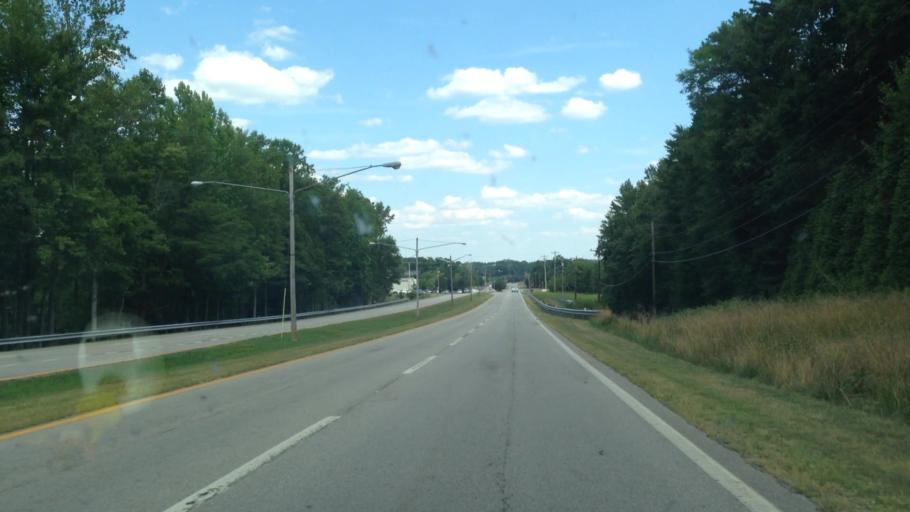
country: US
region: Virginia
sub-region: City of Danville
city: Danville
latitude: 36.5941
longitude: -79.4671
